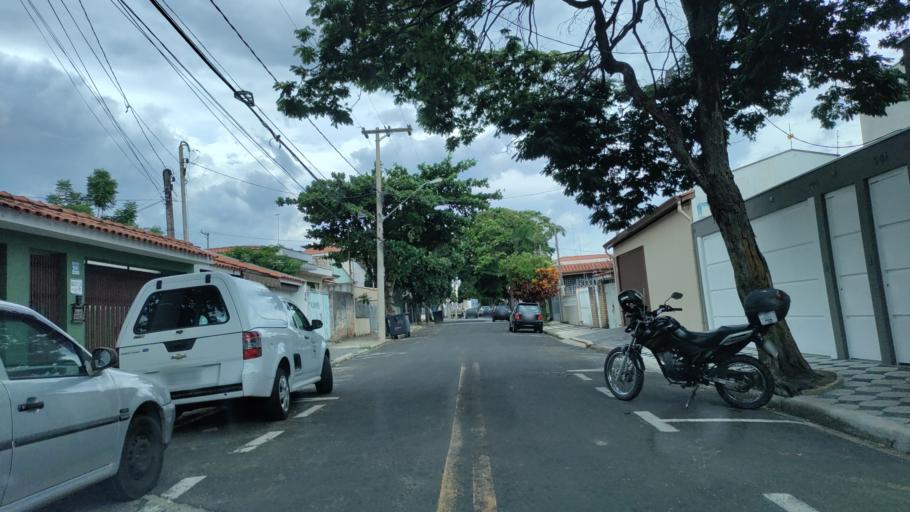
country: BR
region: Sao Paulo
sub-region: Sorocaba
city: Sorocaba
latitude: -23.4942
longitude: -47.4674
